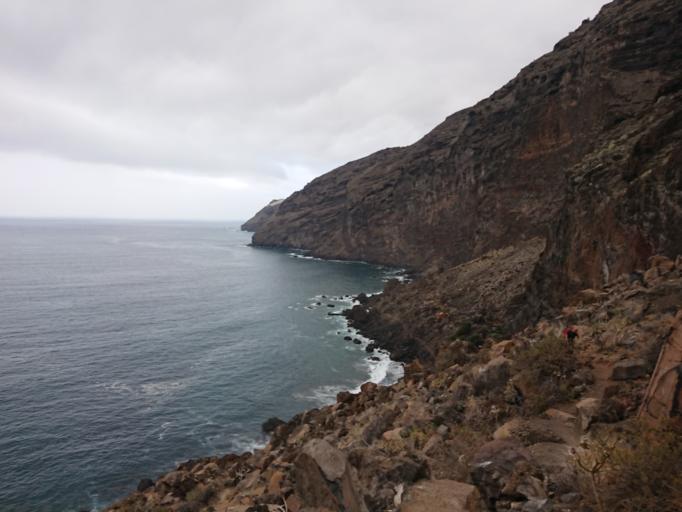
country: ES
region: Canary Islands
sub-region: Provincia de Santa Cruz de Tenerife
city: Tijarafe
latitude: 28.7194
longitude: -17.9790
